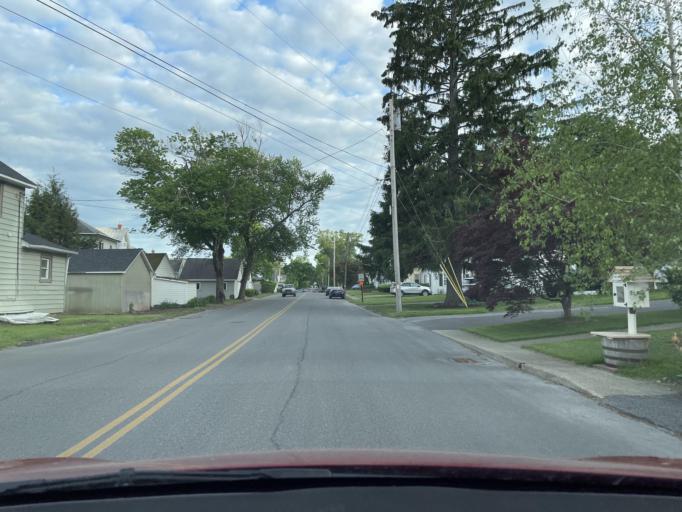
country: US
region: New York
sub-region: Ulster County
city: Saugerties
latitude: 42.0847
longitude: -73.9564
